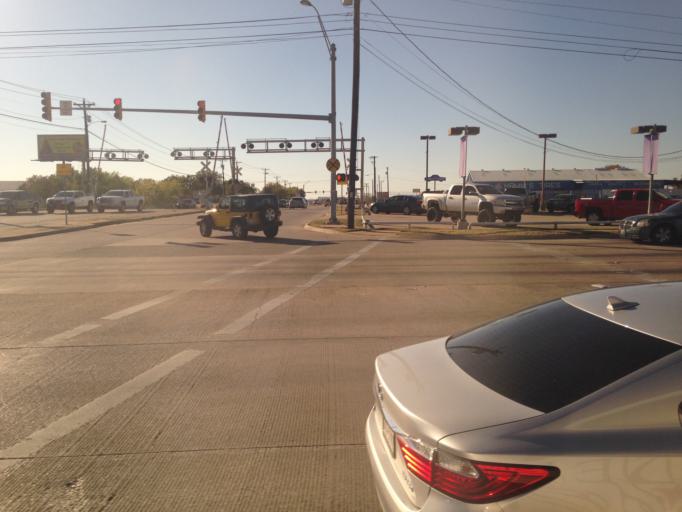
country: US
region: Texas
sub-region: Tarrant County
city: Watauga
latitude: 32.8607
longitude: -97.2638
